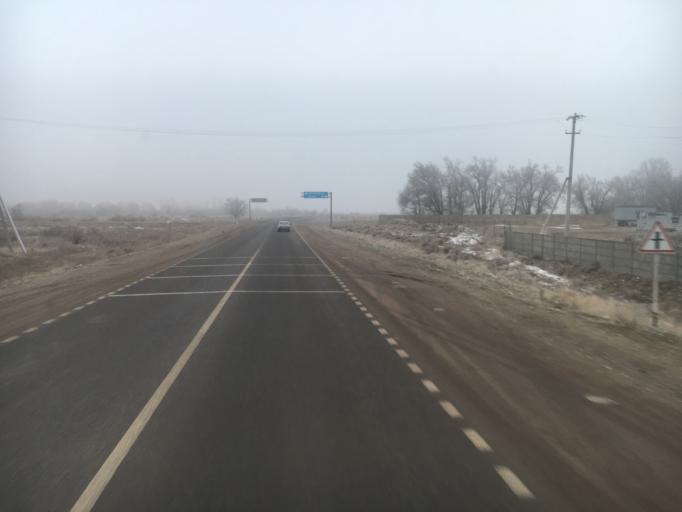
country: KZ
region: Zhambyl
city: Sarykemer
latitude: 43.0404
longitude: 71.5352
